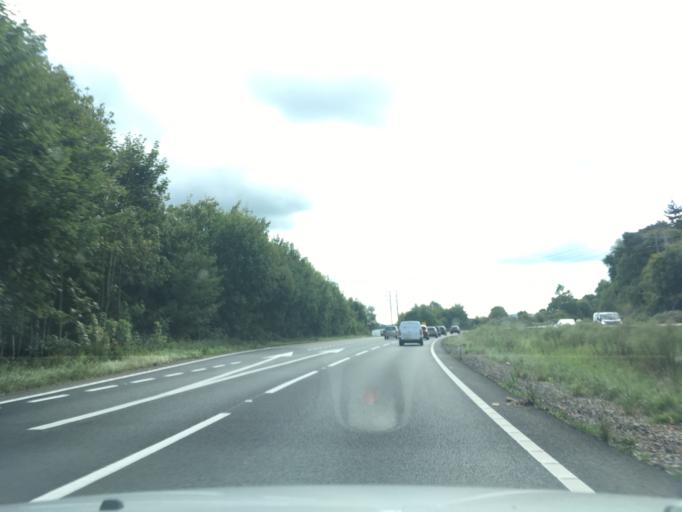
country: GB
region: England
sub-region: Surrey
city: Milford
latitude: 51.1996
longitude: -0.6463
